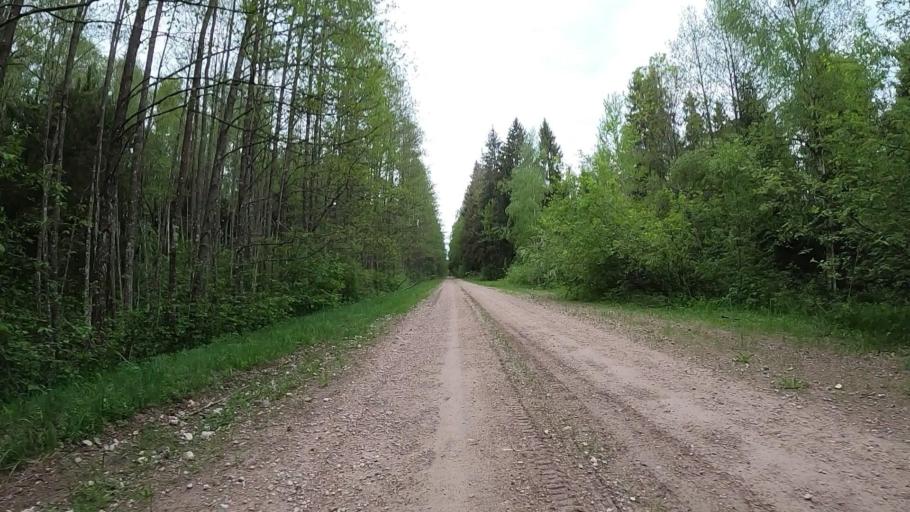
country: LV
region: Ozolnieku
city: Ozolnieki
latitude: 56.7997
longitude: 23.7832
